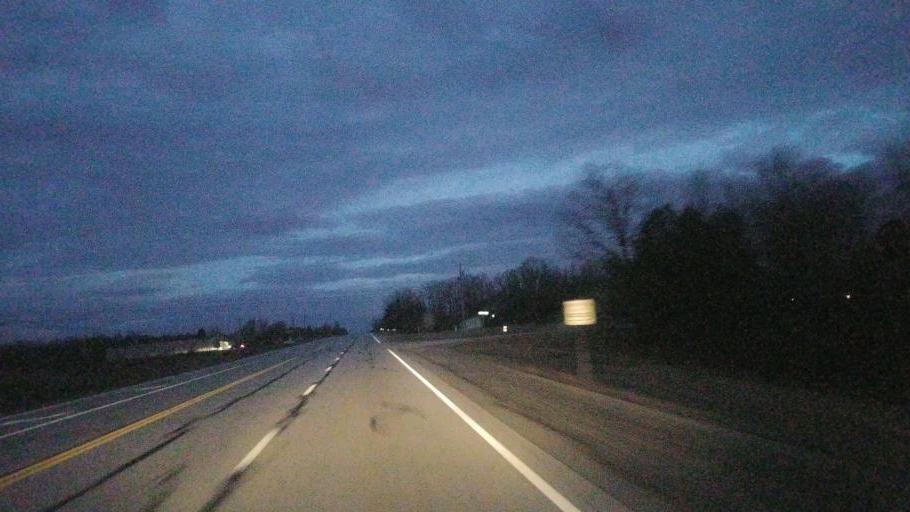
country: US
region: Tennessee
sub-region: Sequatchie County
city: Dunlap
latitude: 35.4773
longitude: -85.4624
